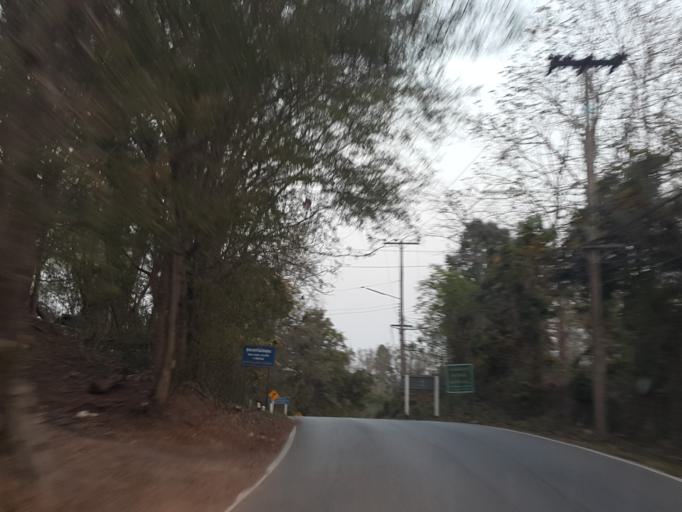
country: TH
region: Chiang Mai
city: Mae Taeng
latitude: 18.9896
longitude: 98.9001
